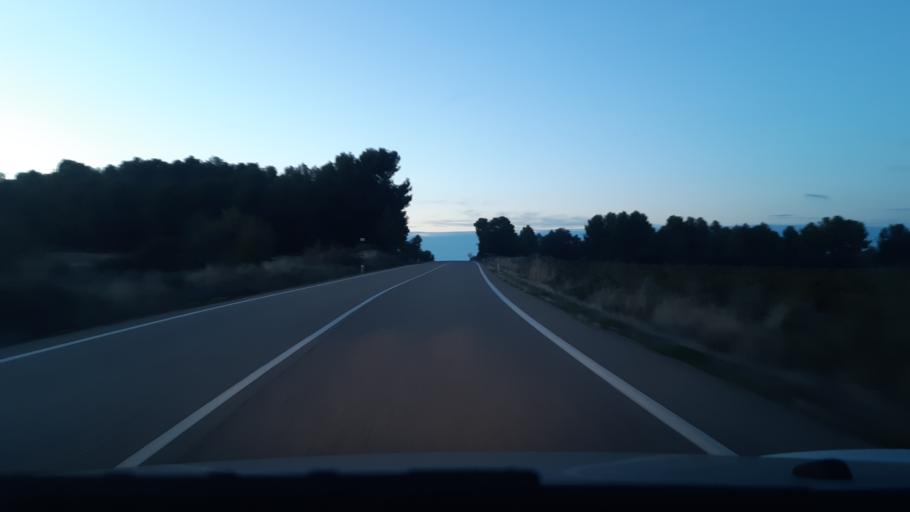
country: ES
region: Aragon
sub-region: Provincia de Teruel
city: Lledo
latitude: 40.9540
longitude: 0.2218
